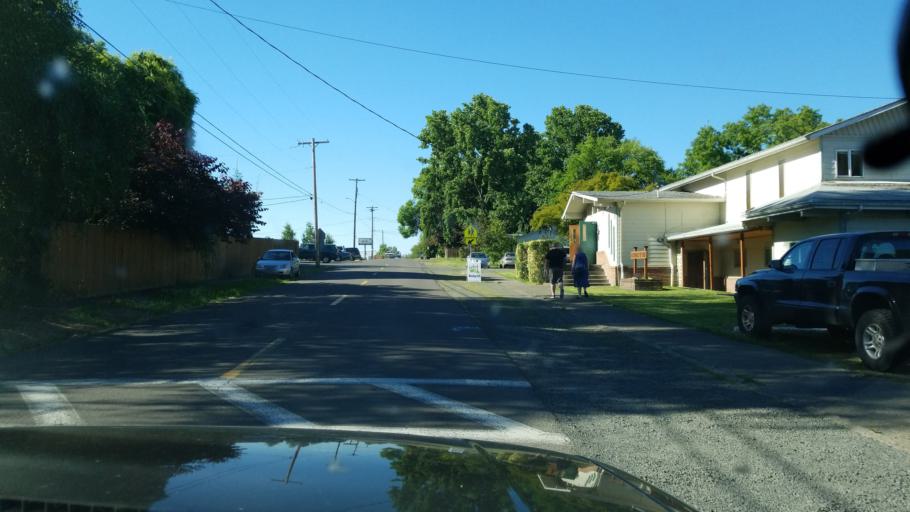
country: US
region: Oregon
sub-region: Yamhill County
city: Carlton
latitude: 45.2919
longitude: -123.1736
